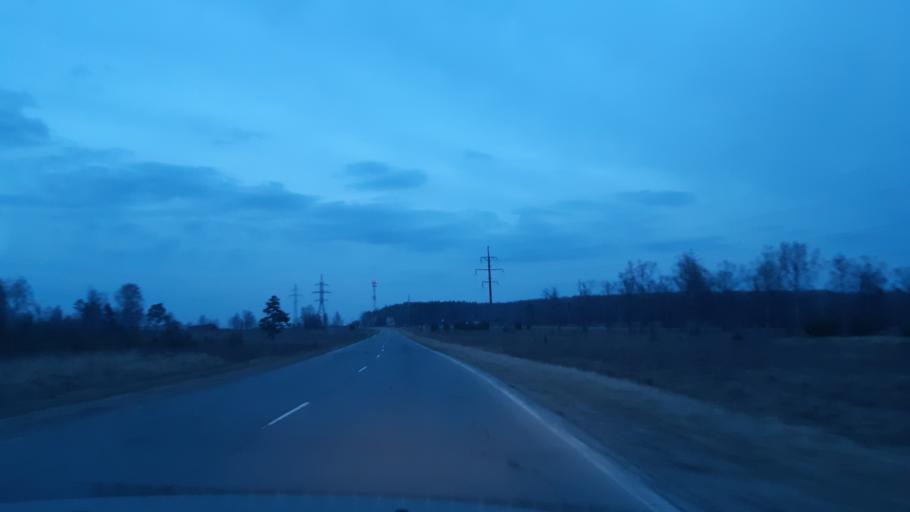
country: RU
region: Vladimir
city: Luknovo
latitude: 56.1946
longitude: 42.0309
